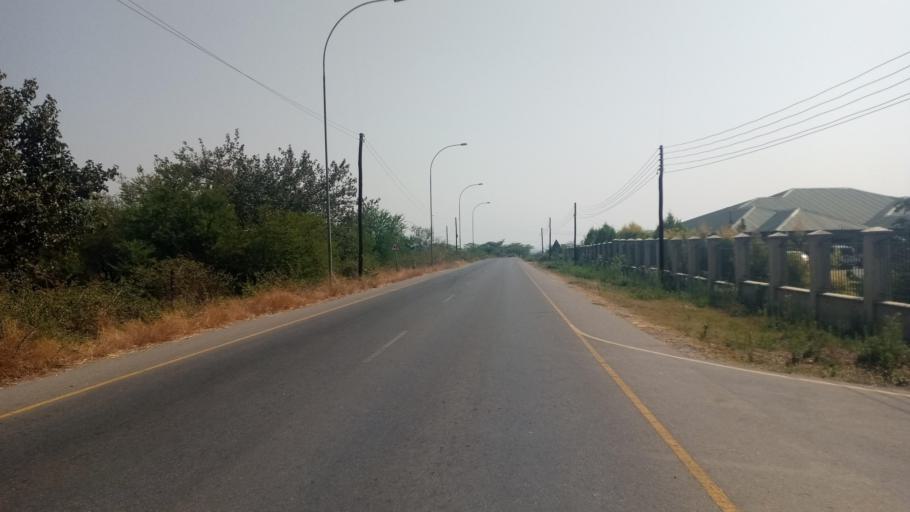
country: ZM
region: Lusaka
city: Lusaka
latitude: -15.4536
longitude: 28.4352
